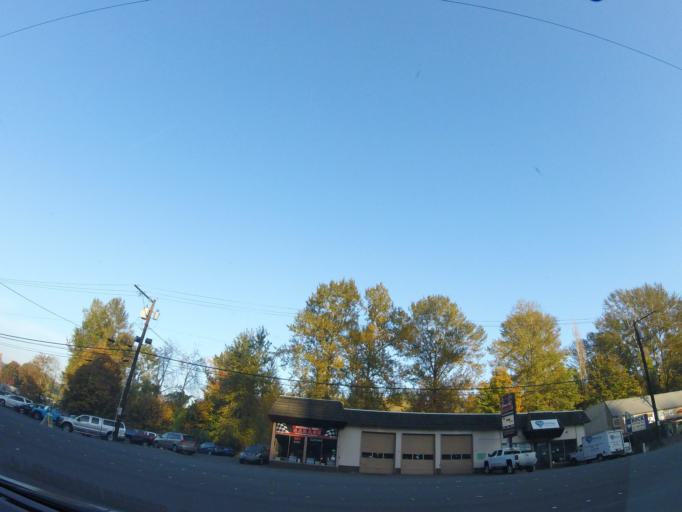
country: US
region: Washington
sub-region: King County
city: Bothell
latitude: 47.7531
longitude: -122.2127
